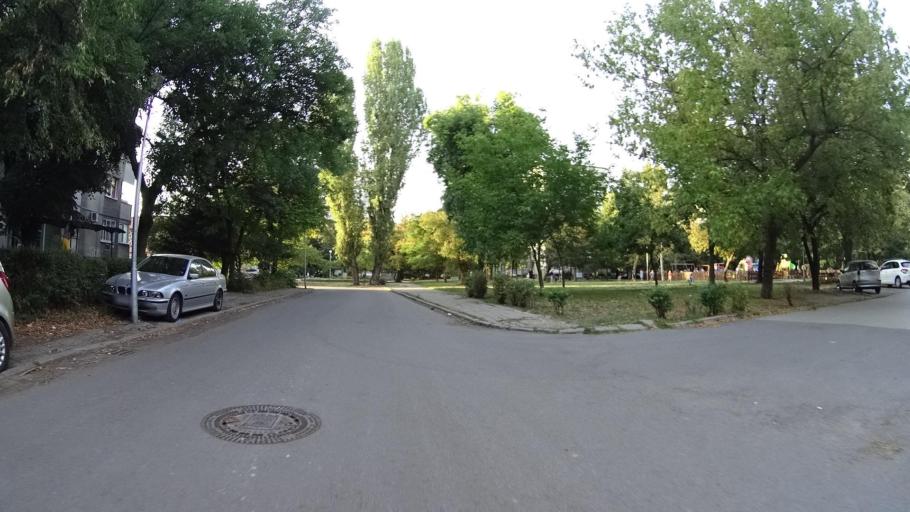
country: BG
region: Plovdiv
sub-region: Obshtina Plovdiv
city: Plovdiv
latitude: 42.1315
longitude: 24.7471
